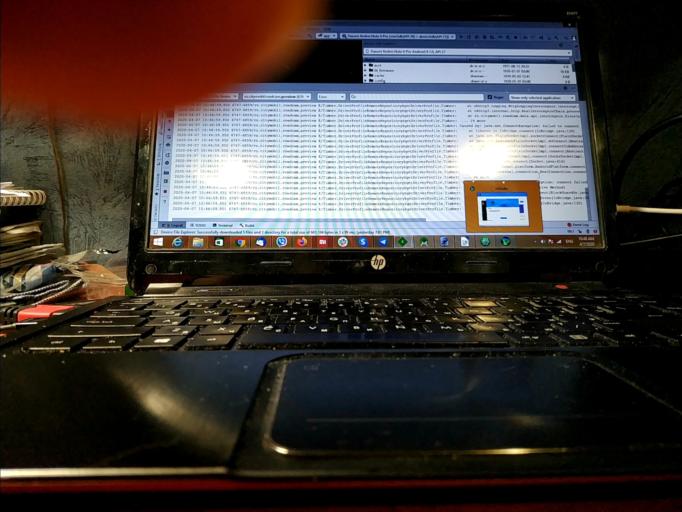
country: RU
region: Vologda
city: Suda
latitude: 58.9222
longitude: 37.5432
